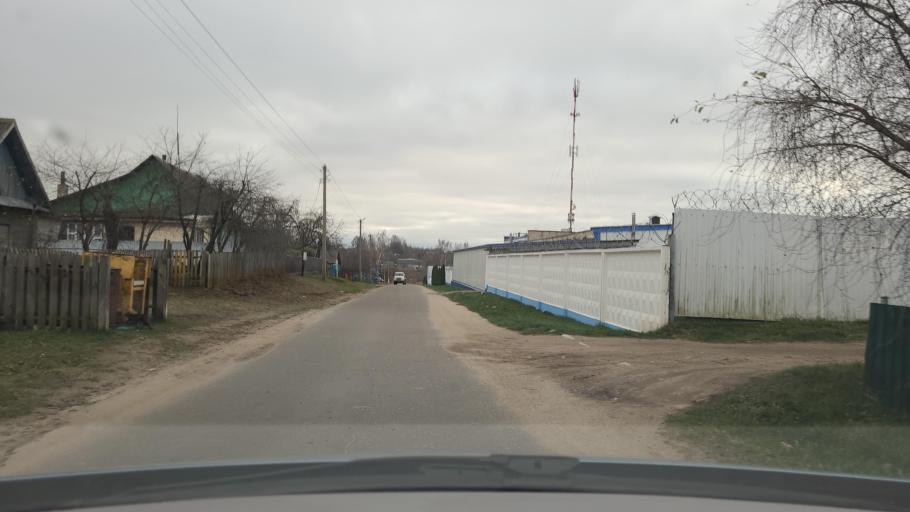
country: BY
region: Minsk
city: Khalopyenichy
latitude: 54.5160
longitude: 28.9549
